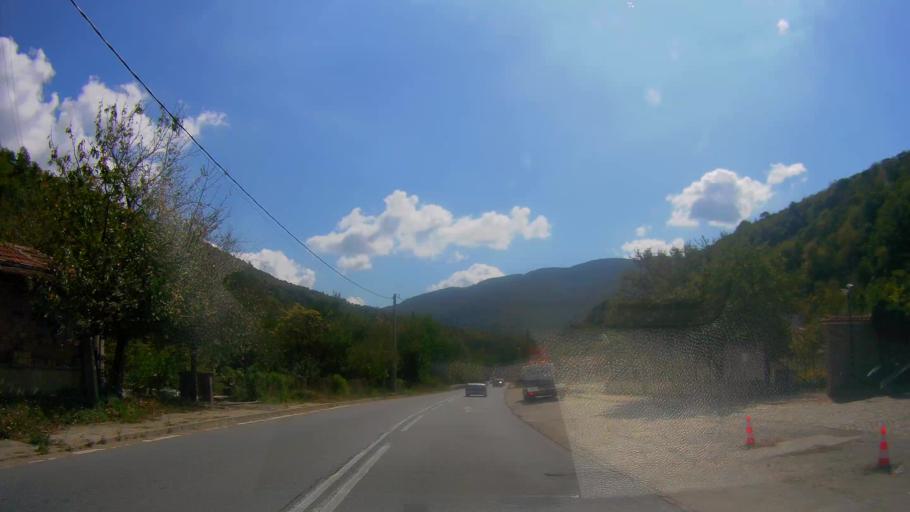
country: BG
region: Stara Zagora
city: Gurkovo
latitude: 42.7176
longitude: 25.7166
